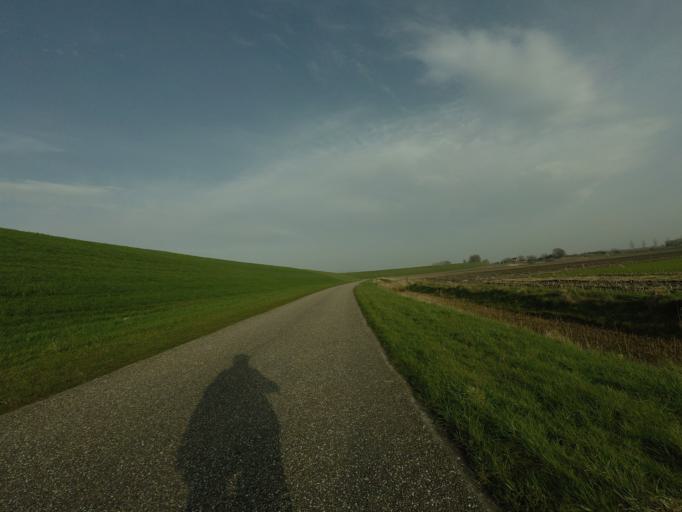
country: NL
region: Zeeland
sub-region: Gemeente Reimerswaal
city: Yerseke
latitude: 51.4057
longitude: 3.9883
